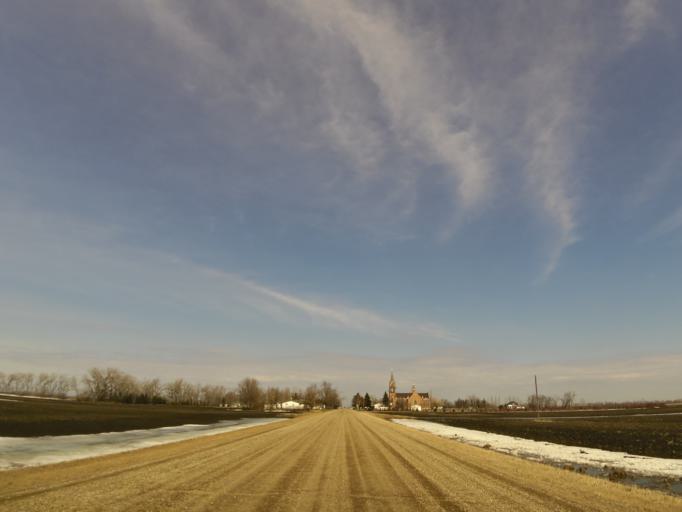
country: US
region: North Dakota
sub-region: Walsh County
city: Grafton
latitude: 48.2902
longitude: -97.2547
